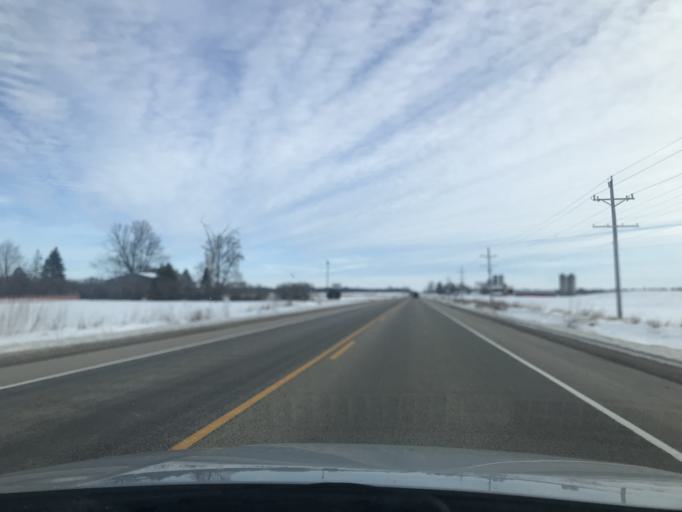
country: US
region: Wisconsin
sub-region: Oconto County
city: Gillett
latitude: 44.8959
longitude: -88.2361
